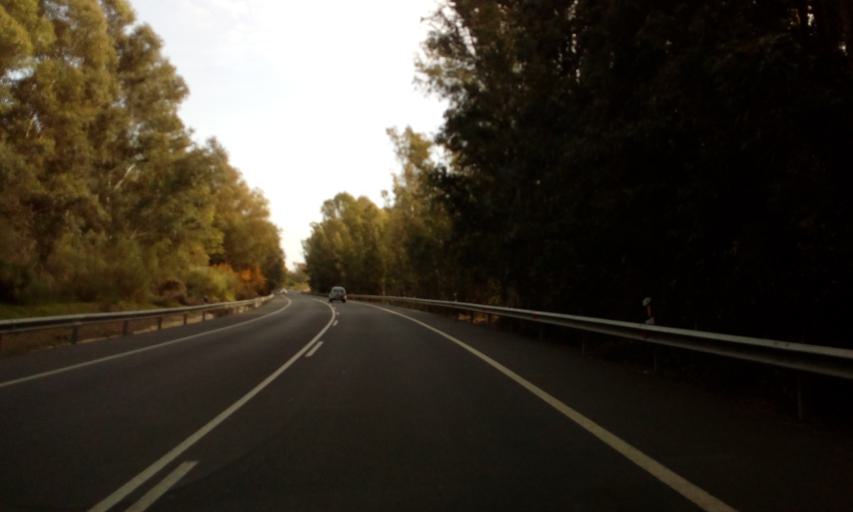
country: ES
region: Andalusia
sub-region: Provincia de Huelva
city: Palos de la Frontera
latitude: 37.1629
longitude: -6.8877
